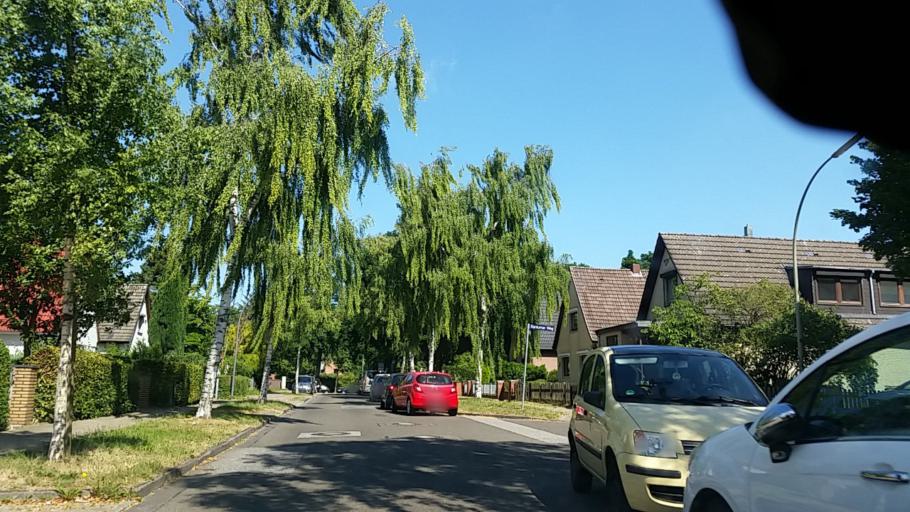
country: DE
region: Schleswig-Holstein
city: Oststeinbek
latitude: 53.5401
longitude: 10.1381
